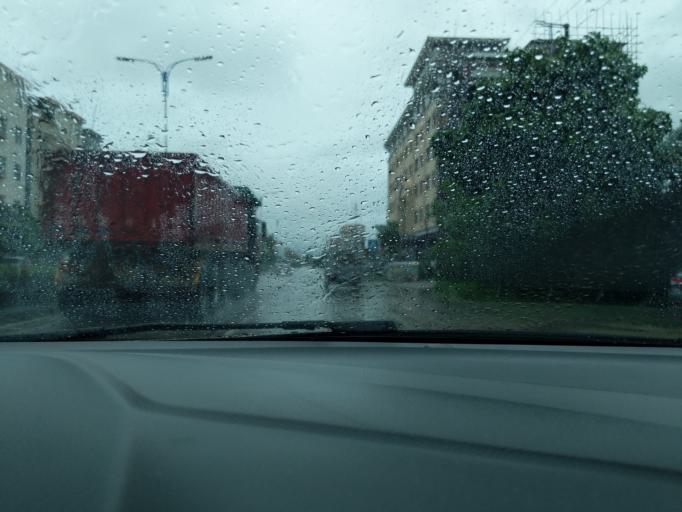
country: CN
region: Guangdong
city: Pingshi
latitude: 22.2057
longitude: 112.3259
